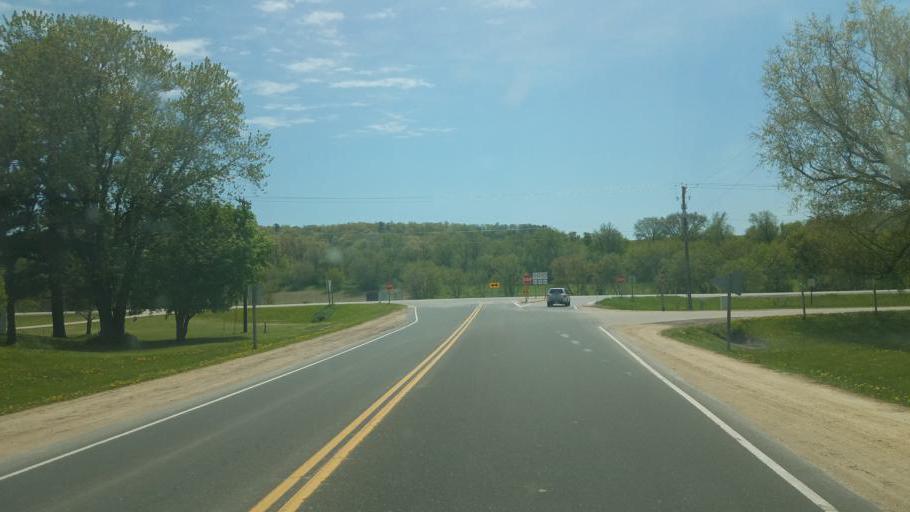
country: US
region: Wisconsin
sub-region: Monroe County
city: Tomah
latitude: 43.8337
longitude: -90.4740
